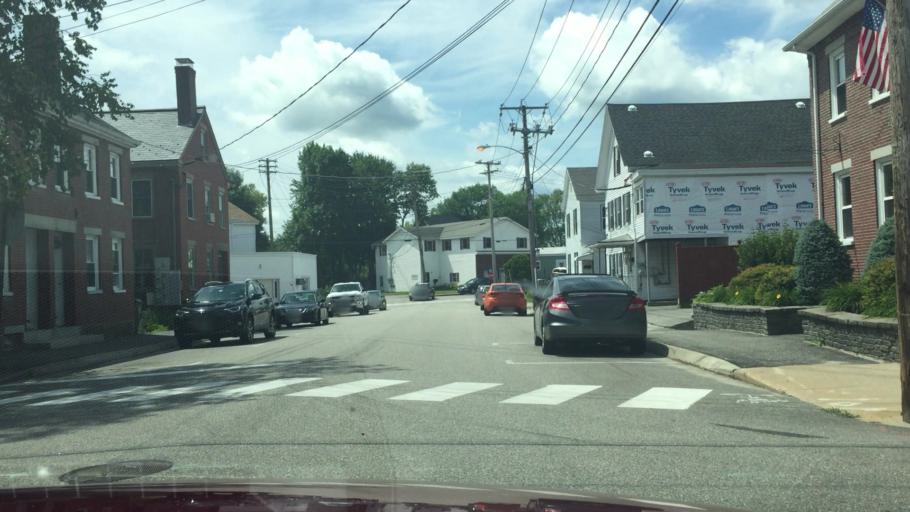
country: US
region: Maine
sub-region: York County
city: Saco
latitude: 43.4972
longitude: -70.4450
